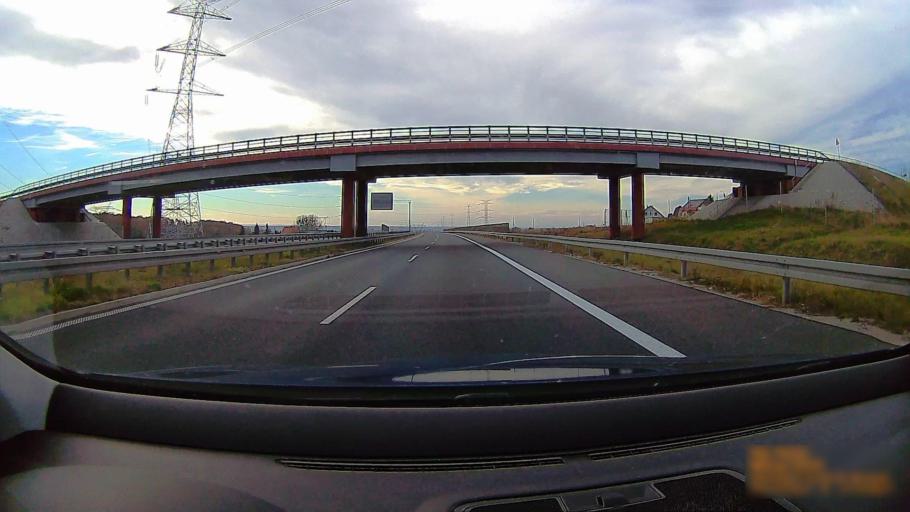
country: PL
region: Greater Poland Voivodeship
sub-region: Powiat ostrowski
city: Przygodzice
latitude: 51.6230
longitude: 17.8633
